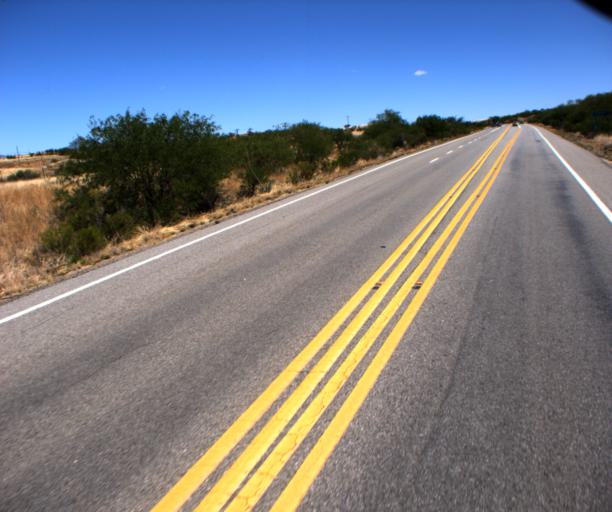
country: US
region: Arizona
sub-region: Santa Cruz County
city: Rio Rico
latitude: 31.4622
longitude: -110.8255
